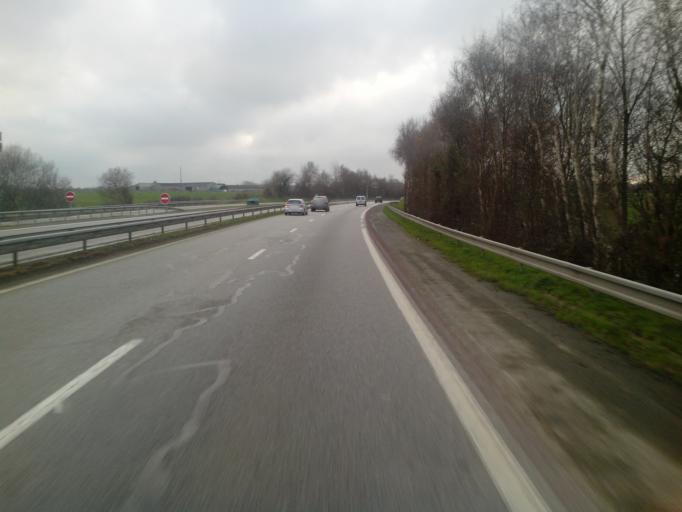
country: FR
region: Brittany
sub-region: Departement du Morbihan
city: Guegon
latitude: 47.9337
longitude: -2.6288
